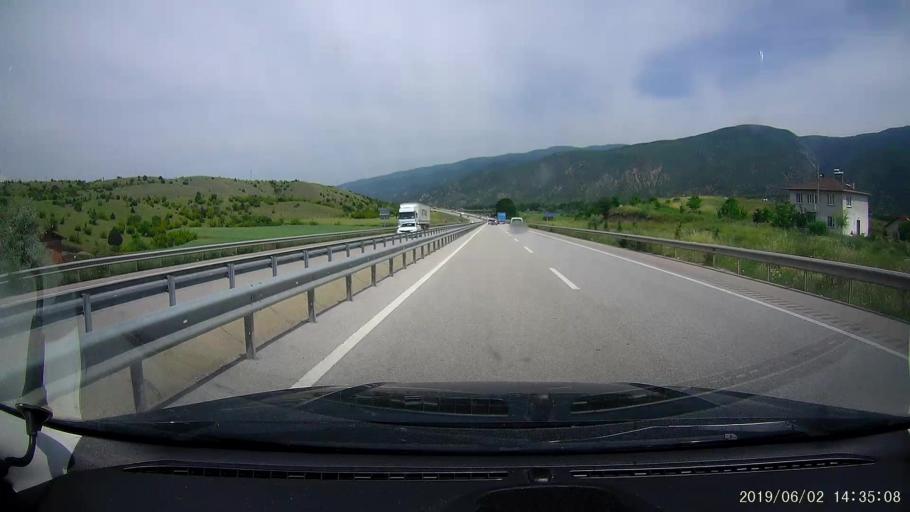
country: TR
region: Kastamonu
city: Tosya
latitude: 41.0405
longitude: 34.2068
